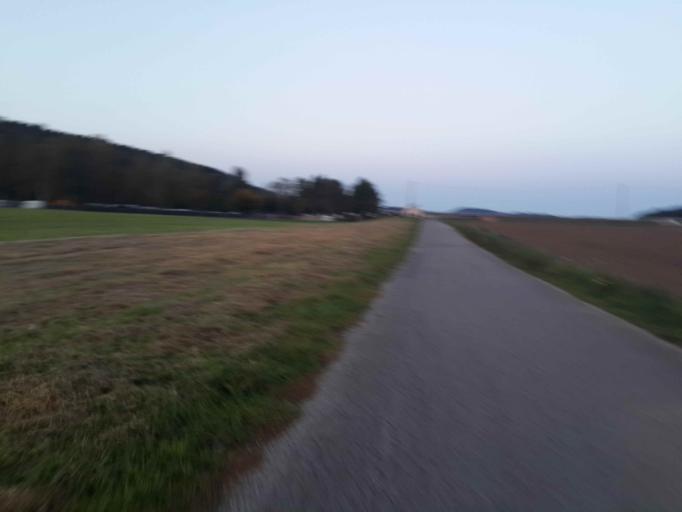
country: DE
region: Bavaria
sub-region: Regierungsbezirk Unterfranken
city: Kreuzwertheim
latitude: 49.7784
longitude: 9.5618
